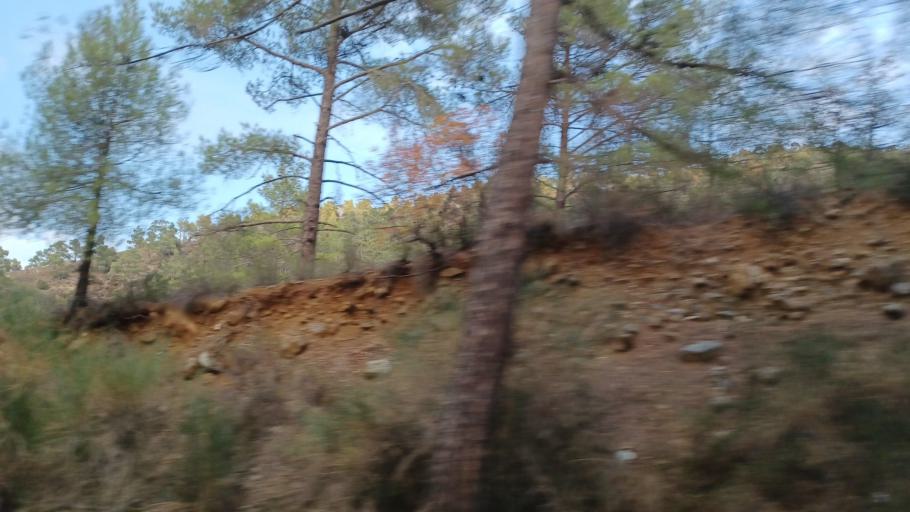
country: CY
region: Lefkosia
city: Kakopetria
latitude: 34.9665
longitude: 32.9222
